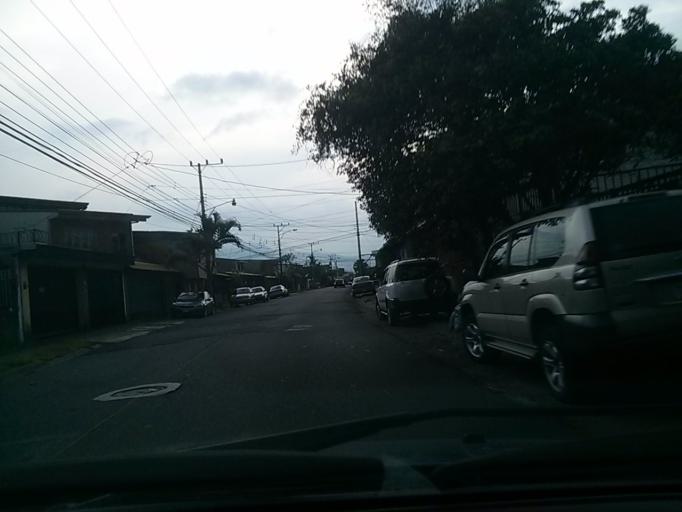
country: CR
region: San Jose
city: San Pedro
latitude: 9.9308
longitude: -84.0390
